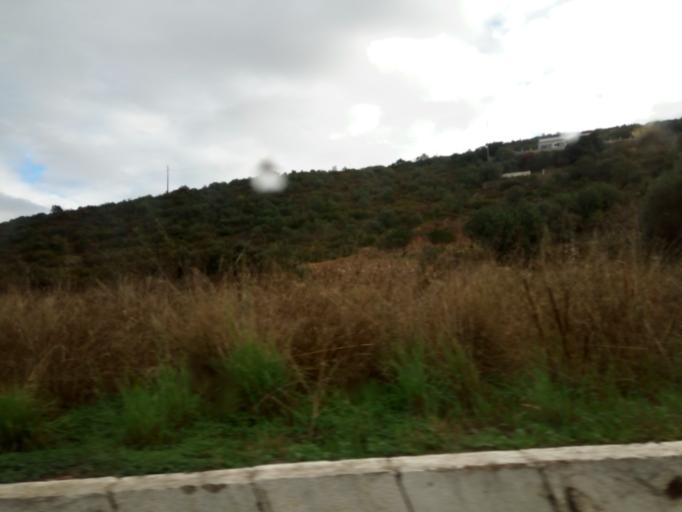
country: PT
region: Faro
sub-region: Loule
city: Loule
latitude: 37.1140
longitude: -8.0082
